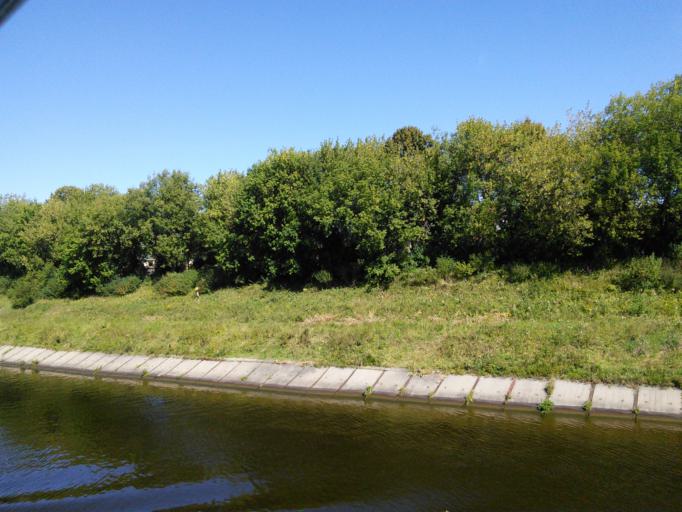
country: RU
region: Moskovskaya
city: Iksha
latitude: 56.1556
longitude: 37.5117
